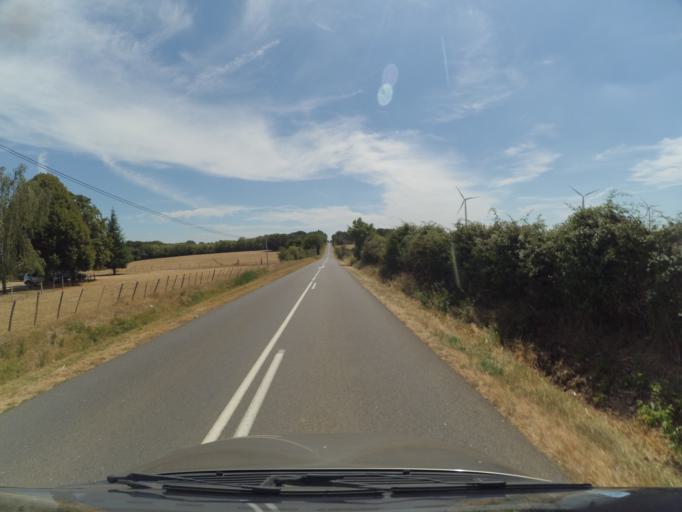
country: FR
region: Poitou-Charentes
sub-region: Departement de la Vienne
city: Usson-du-Poitou
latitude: 46.2383
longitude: 0.5264
